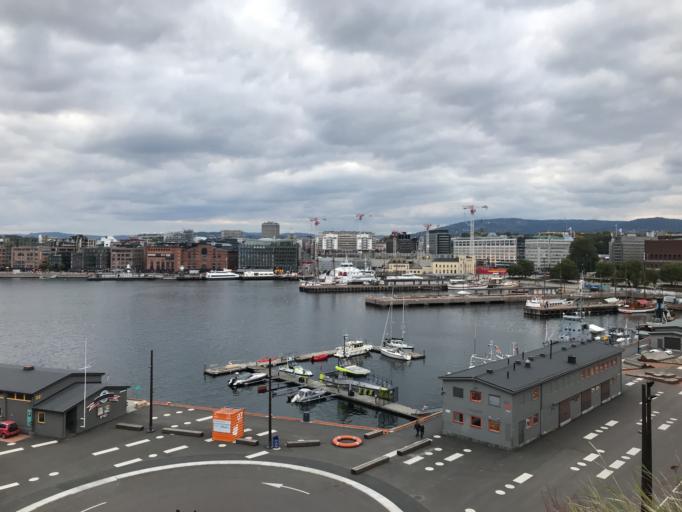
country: NO
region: Oslo
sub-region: Oslo
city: Oslo
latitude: 59.9078
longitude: 10.7352
